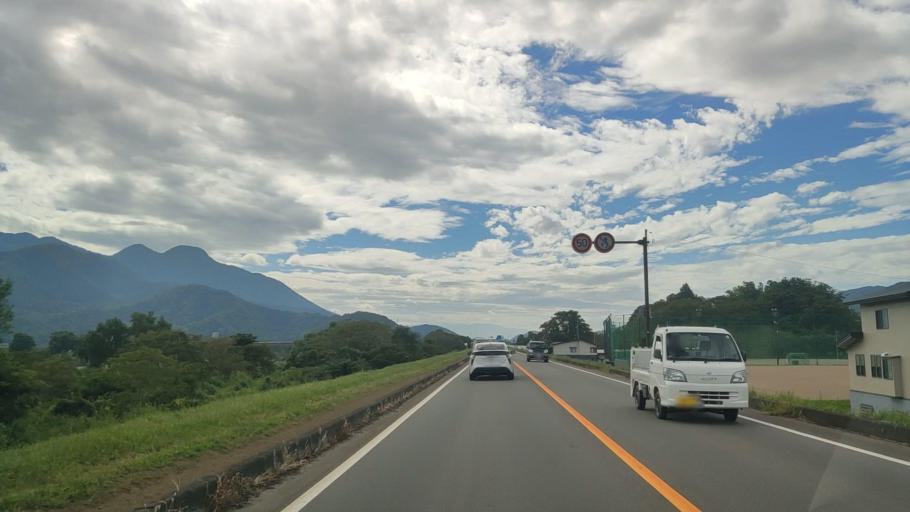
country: JP
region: Nagano
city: Iiyama
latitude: 36.8597
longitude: 138.3691
